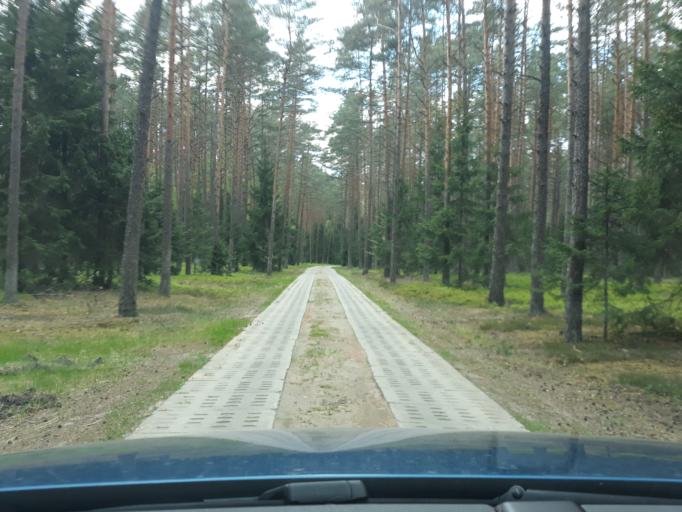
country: PL
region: Pomeranian Voivodeship
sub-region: Powiat czluchowski
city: Czluchow
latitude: 53.7436
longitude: 17.3428
